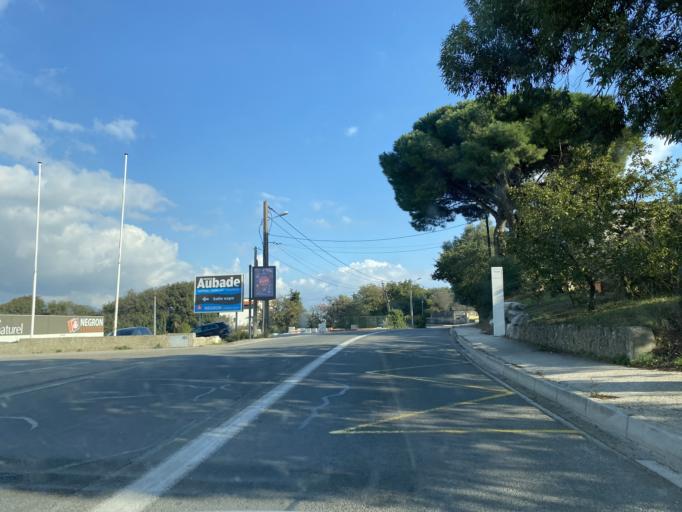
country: FR
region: Provence-Alpes-Cote d'Azur
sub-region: Departement du Var
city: Six-Fours-les-Plages
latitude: 43.1082
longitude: 5.8378
